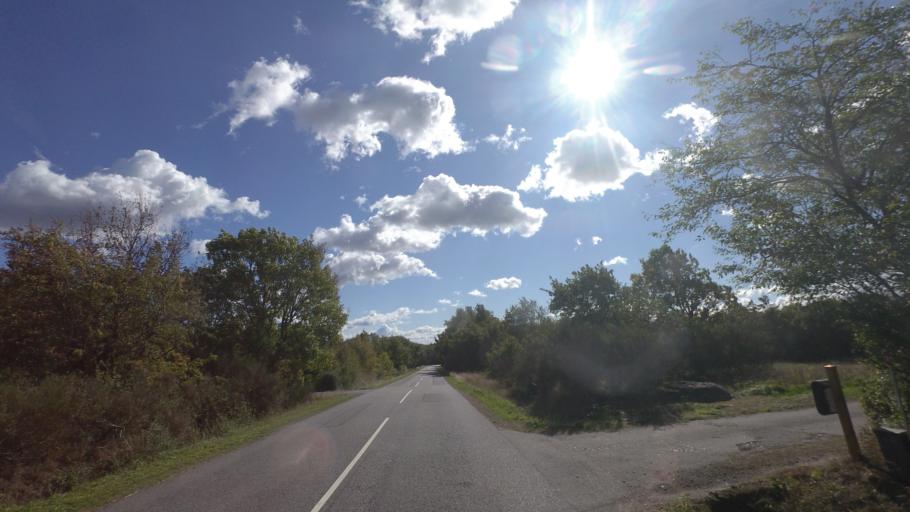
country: DK
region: Capital Region
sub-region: Bornholm Kommune
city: Nexo
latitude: 55.0695
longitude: 15.0825
